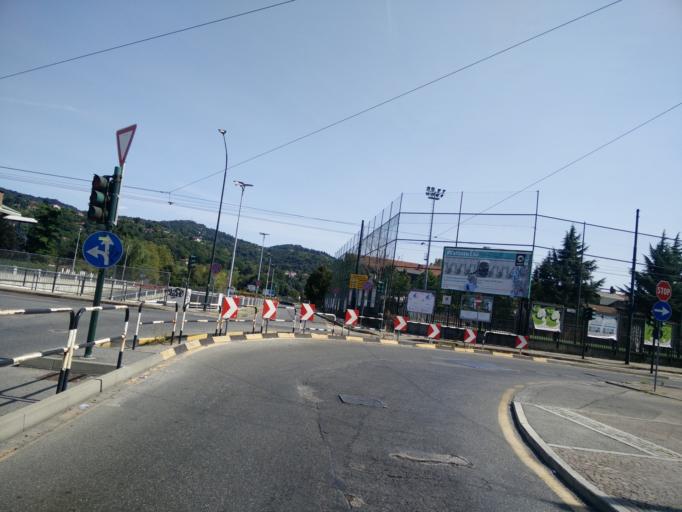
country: IT
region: Piedmont
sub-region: Provincia di Torino
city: Moncalieri
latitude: 45.0265
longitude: 7.6668
